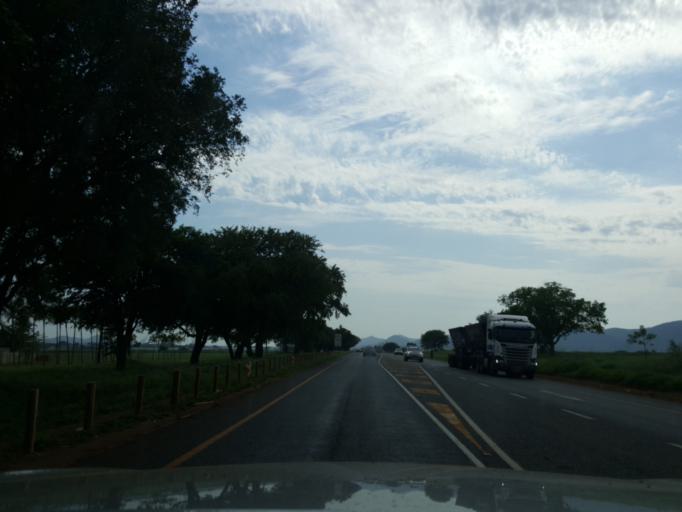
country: SZ
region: Hhohho
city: Ntfonjeni
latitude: -25.5058
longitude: 31.4922
